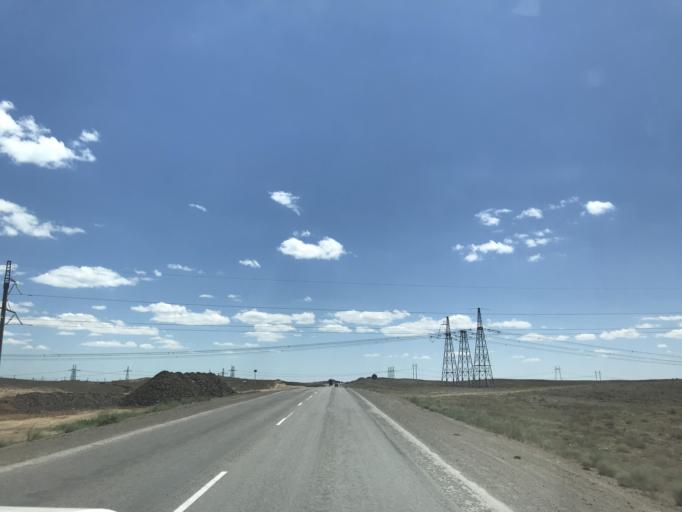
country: KZ
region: Almaty Oblysy
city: Ulken
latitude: 45.1451
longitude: 73.9577
